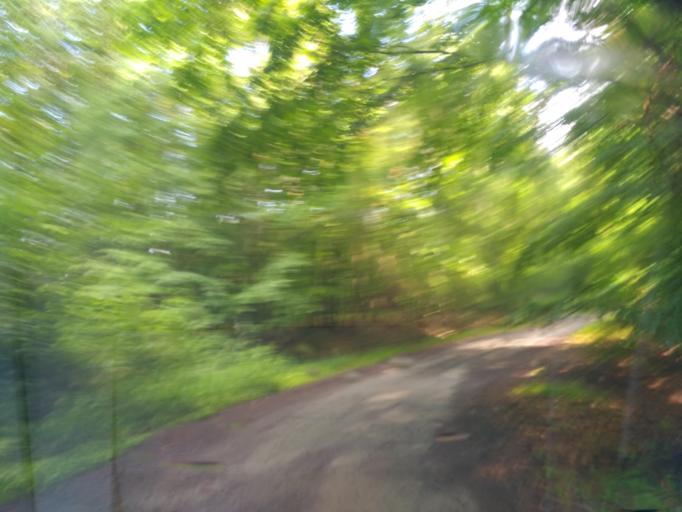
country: SK
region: Kosicky
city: Secovce
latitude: 48.6001
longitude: 21.5131
